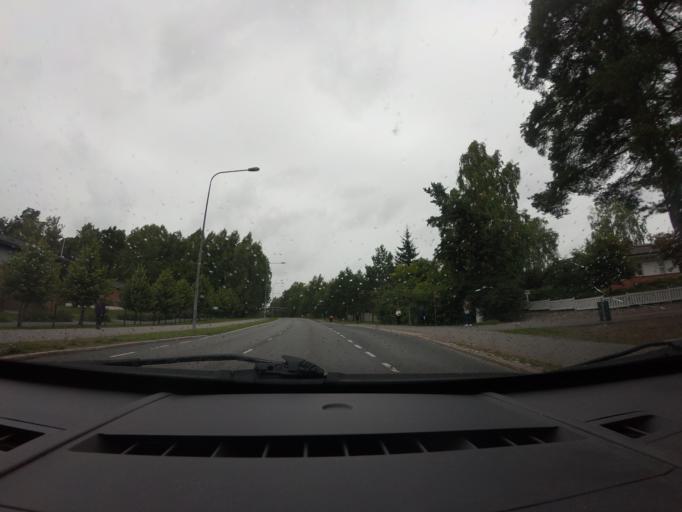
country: FI
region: Varsinais-Suomi
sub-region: Turku
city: Turku
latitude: 60.4156
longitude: 22.3053
